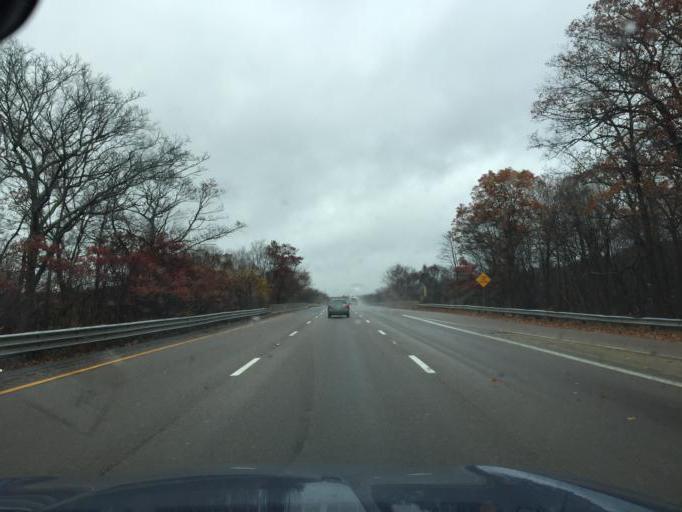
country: US
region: Massachusetts
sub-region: Bristol County
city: Attleboro
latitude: 41.9331
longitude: -71.3198
